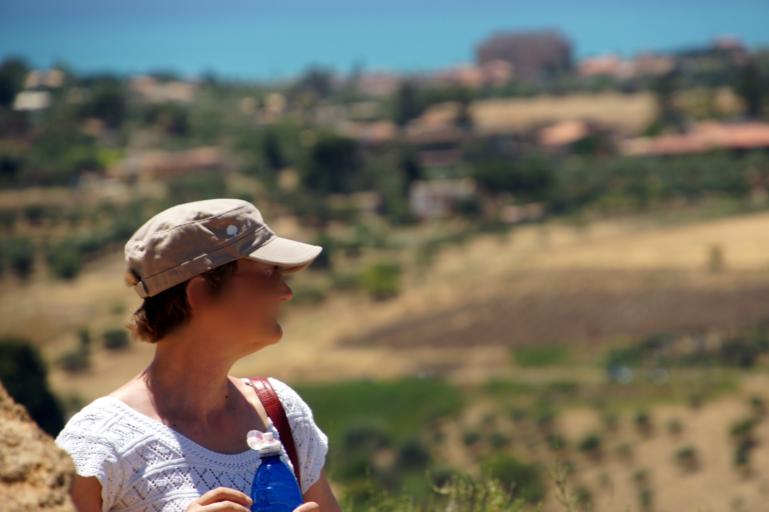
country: IT
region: Sicily
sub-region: Agrigento
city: San Leone Mose
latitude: 37.2885
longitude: 13.5999
